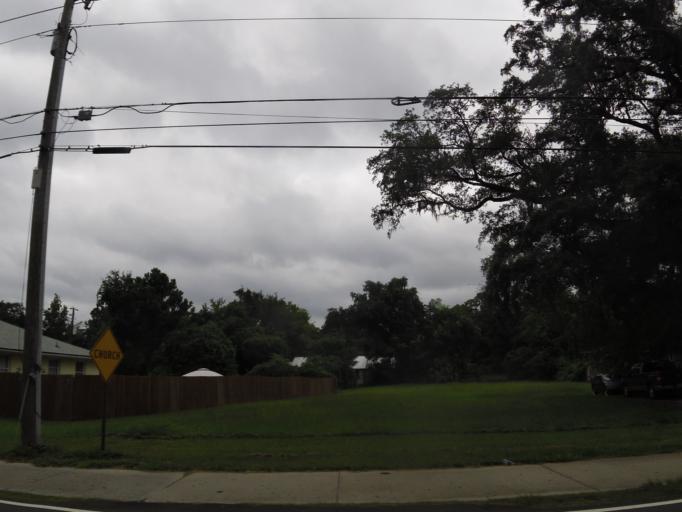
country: US
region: Georgia
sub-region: Glynn County
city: Saint Simon Mills
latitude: 31.1618
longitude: -81.3955
